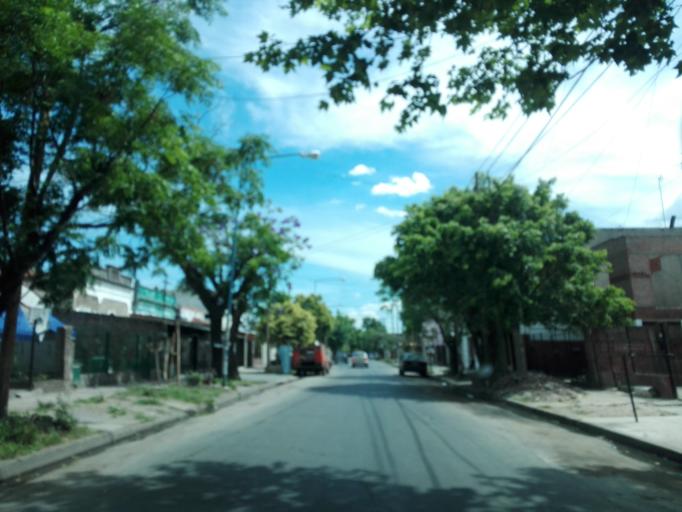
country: AR
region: Buenos Aires
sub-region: Partido de Lanus
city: Lanus
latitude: -34.7220
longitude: -58.3866
